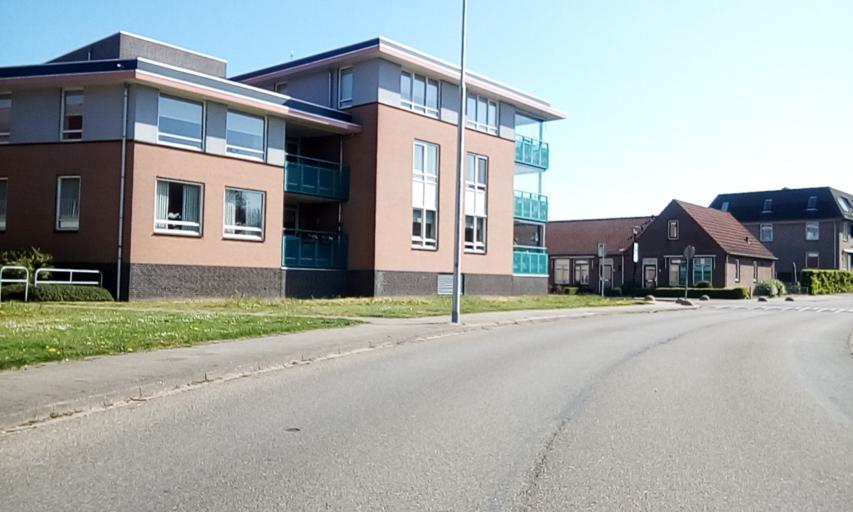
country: NL
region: Gelderland
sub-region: Gemeente Druten
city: Druten
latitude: 51.8902
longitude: 5.6068
